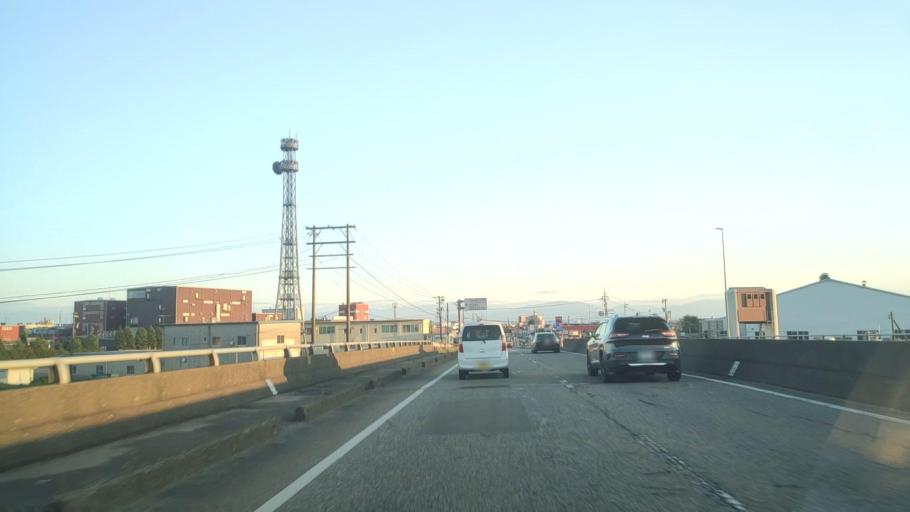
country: JP
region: Toyama
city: Takaoka
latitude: 36.7744
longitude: 137.0004
